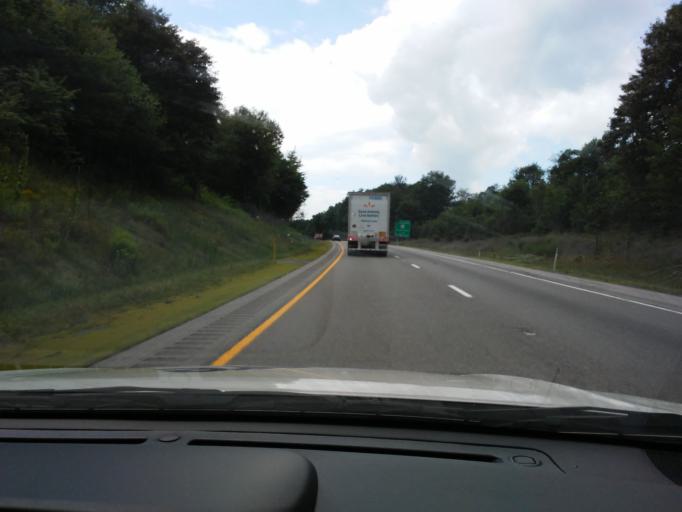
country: US
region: Pennsylvania
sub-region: Centre County
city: Milesburg
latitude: 41.0249
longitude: -77.9115
